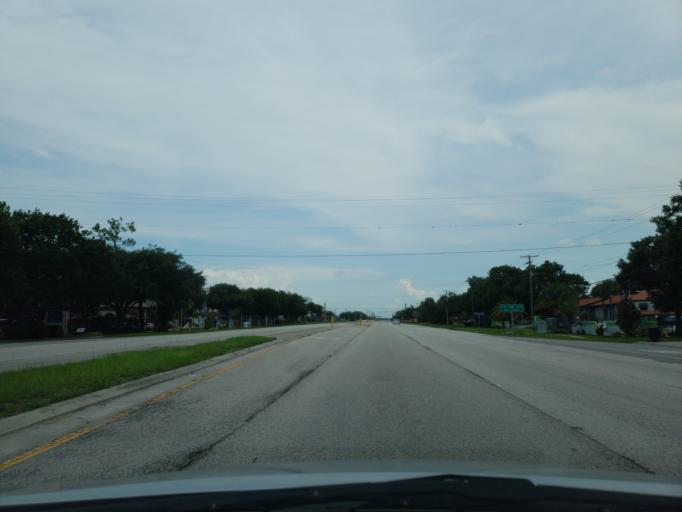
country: US
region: Florida
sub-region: Hillsborough County
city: University
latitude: 28.0761
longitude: -82.4262
